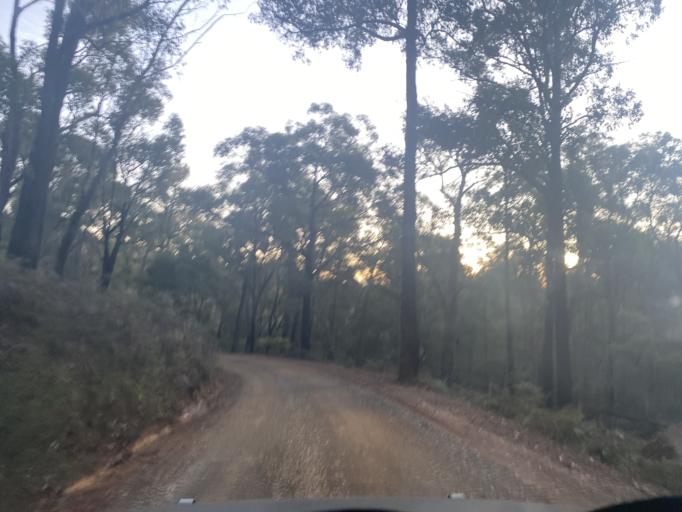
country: AU
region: Victoria
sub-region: Yarra Ranges
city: Healesville
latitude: -37.4325
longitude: 145.5130
